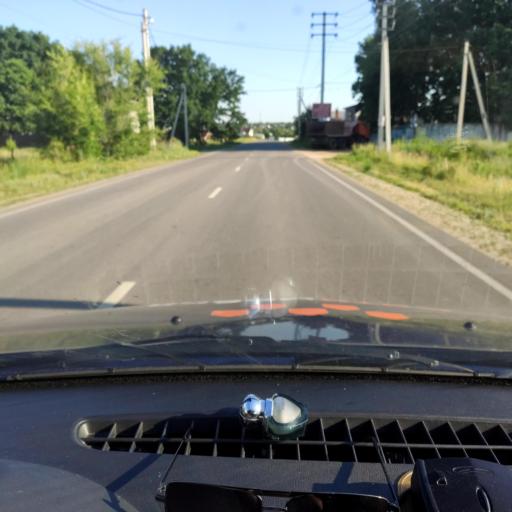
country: RU
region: Voronezj
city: Podgornoye
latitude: 51.8742
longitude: 39.1731
